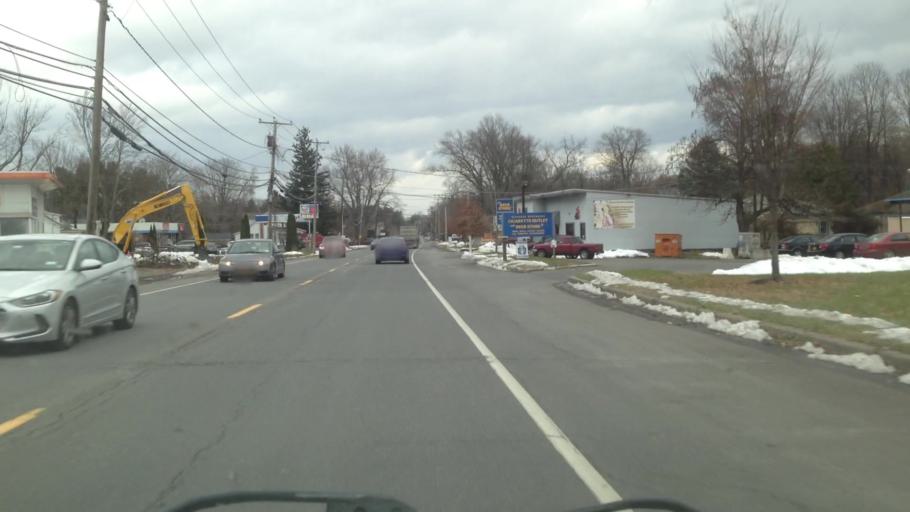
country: US
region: New York
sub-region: Ulster County
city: Saugerties South
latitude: 42.0586
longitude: -73.9537
